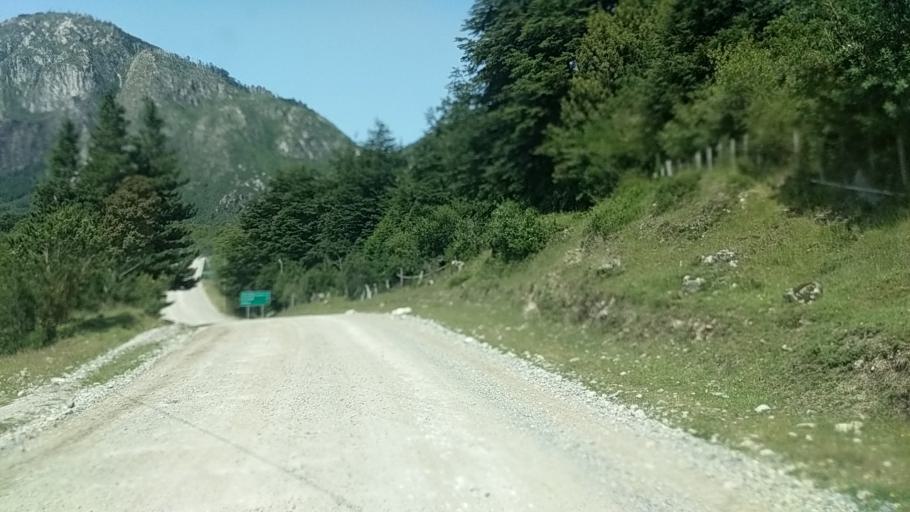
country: CL
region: Los Lagos
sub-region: Provincia de Palena
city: Palena
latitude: -43.4800
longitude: -72.1309
